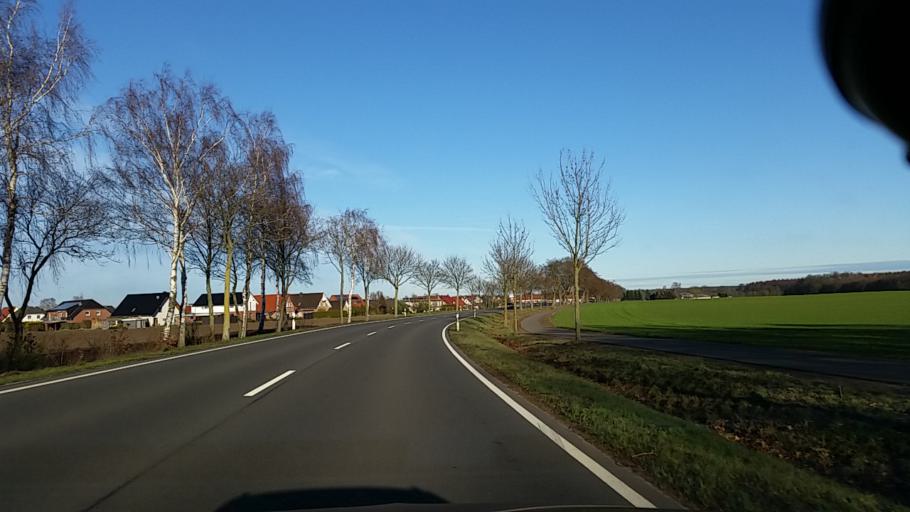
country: DE
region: Lower Saxony
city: Brome
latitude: 52.5896
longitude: 10.9321
